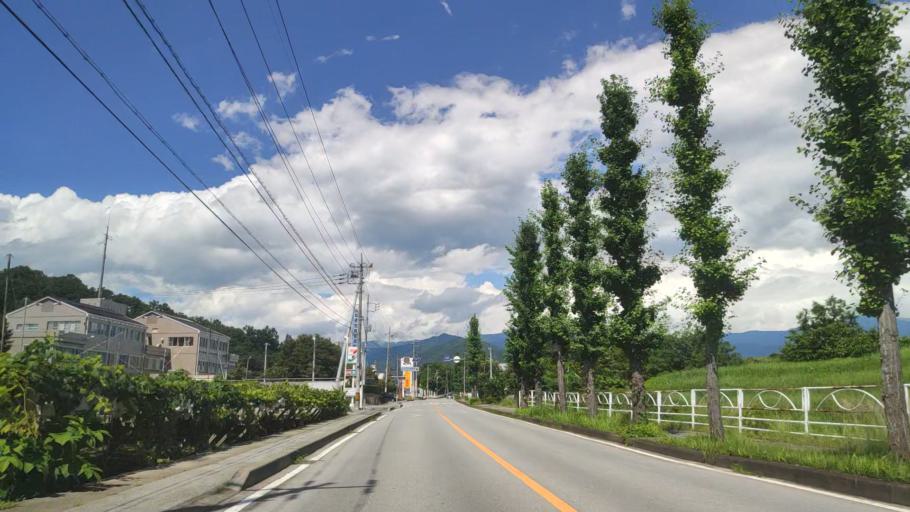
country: JP
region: Yamanashi
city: Enzan
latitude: 35.7043
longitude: 138.6936
